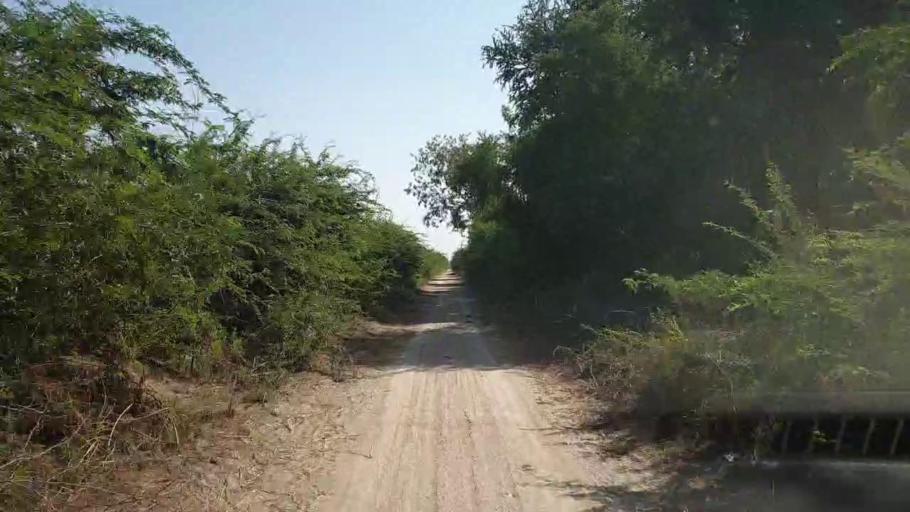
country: PK
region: Sindh
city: Tando Bago
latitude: 24.6405
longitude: 68.9895
